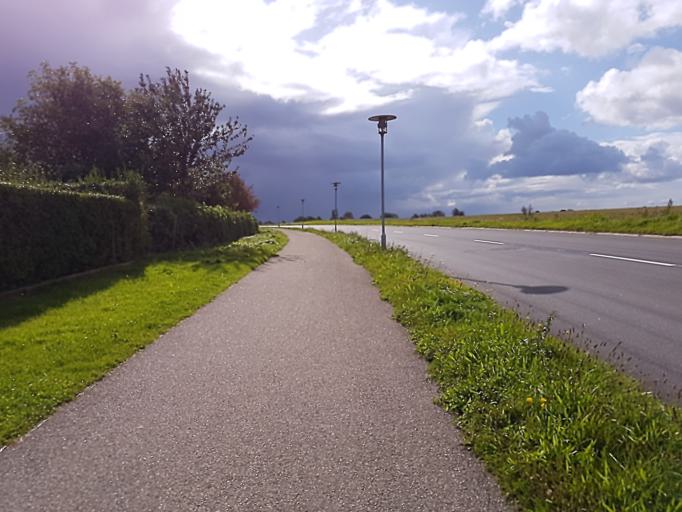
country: DK
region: Zealand
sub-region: Roskilde Kommune
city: Gundsomagle
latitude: 55.7374
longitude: 12.1409
